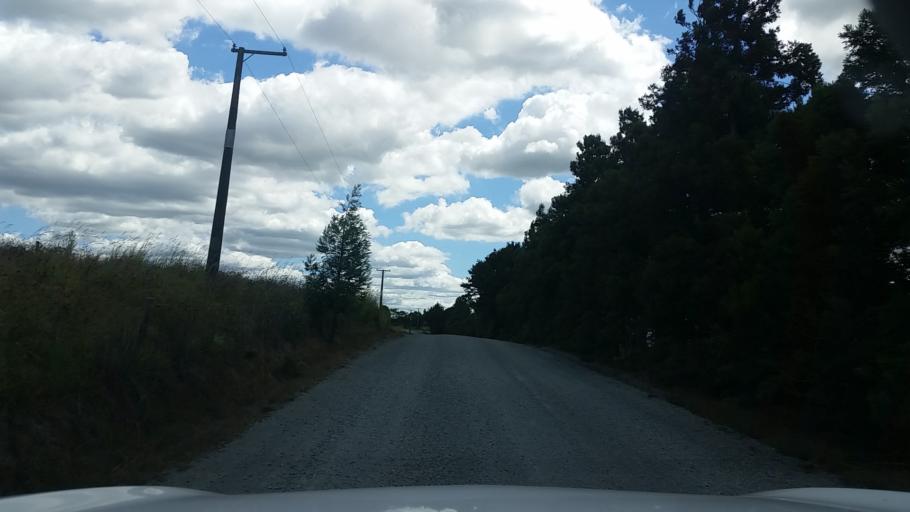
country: NZ
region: Northland
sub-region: Whangarei
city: Maungatapere
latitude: -35.6729
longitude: 174.1580
